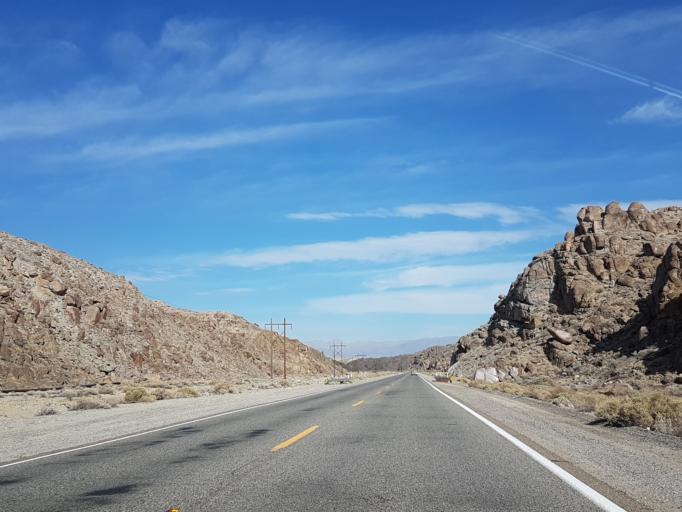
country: US
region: California
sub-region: San Bernardino County
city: Searles Valley
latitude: 35.6575
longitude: -117.4418
